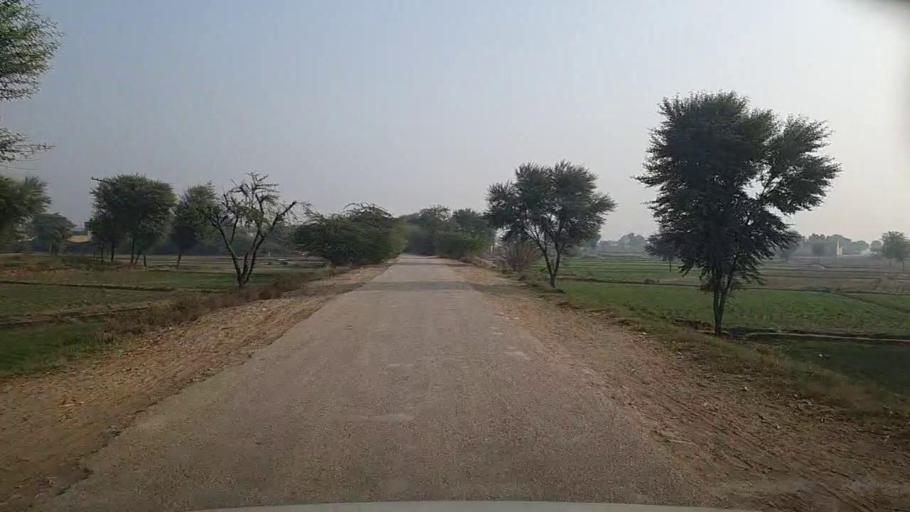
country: PK
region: Sindh
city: Kandiari
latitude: 27.0377
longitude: 68.4803
